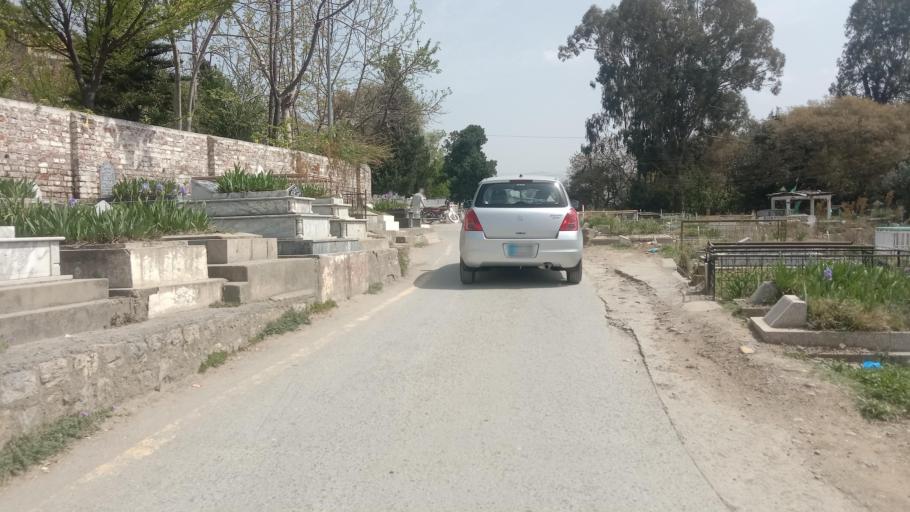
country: PK
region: Khyber Pakhtunkhwa
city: Abbottabad
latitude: 34.1501
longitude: 73.2015
